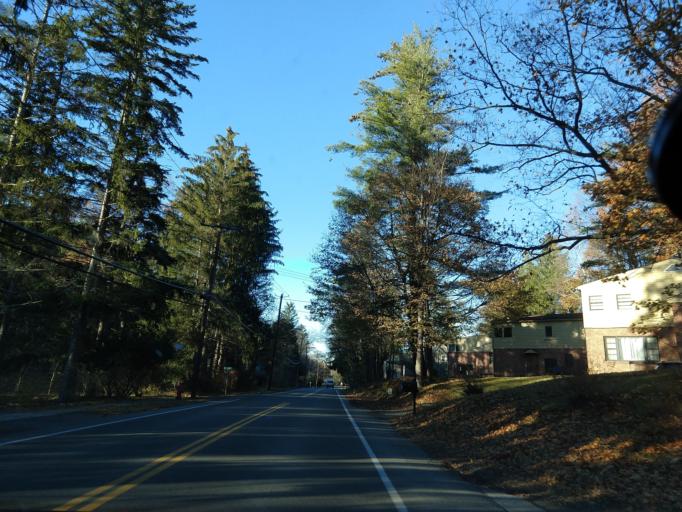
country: US
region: New York
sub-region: Tompkins County
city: Cayuga Heights
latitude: 42.4628
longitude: -76.4834
